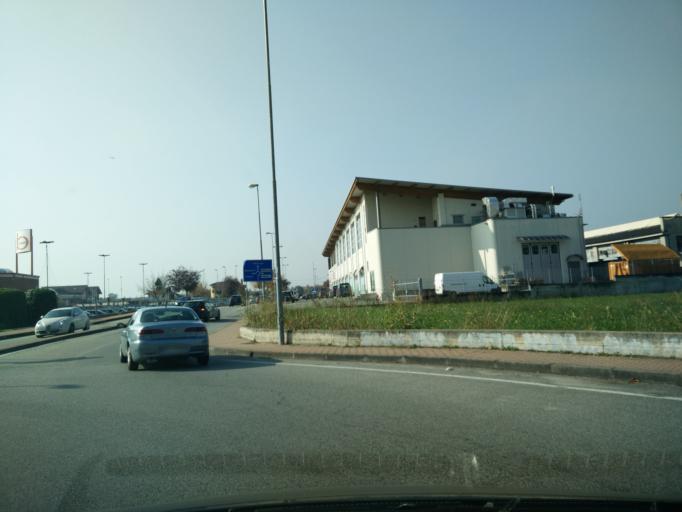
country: IT
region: Piedmont
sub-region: Provincia di Torino
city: Caselle Torinese
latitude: 45.1692
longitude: 7.6547
